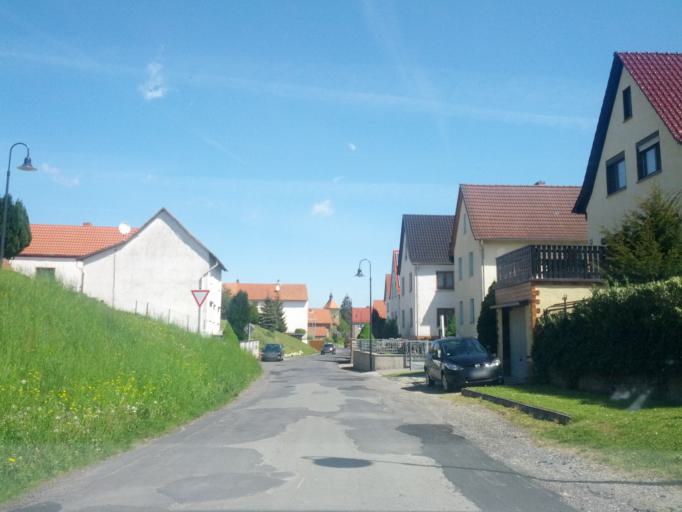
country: DE
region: Thuringia
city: Treffurt
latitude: 51.1023
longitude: 10.2170
